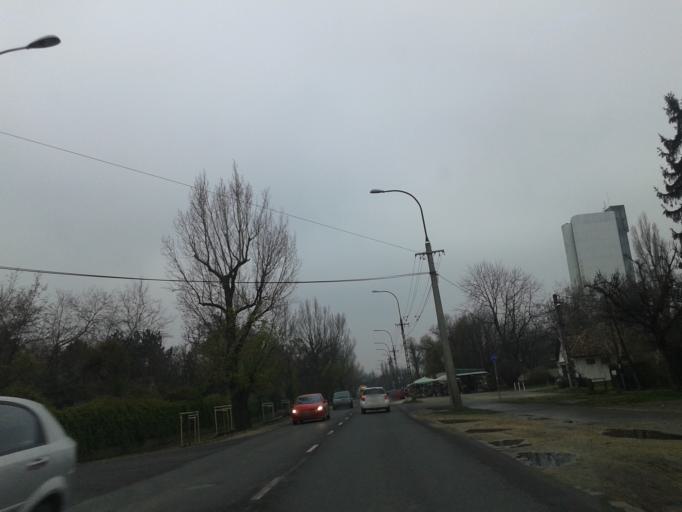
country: HU
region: Budapest
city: Budapest XXII. keruelet
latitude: 47.4072
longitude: 19.0541
